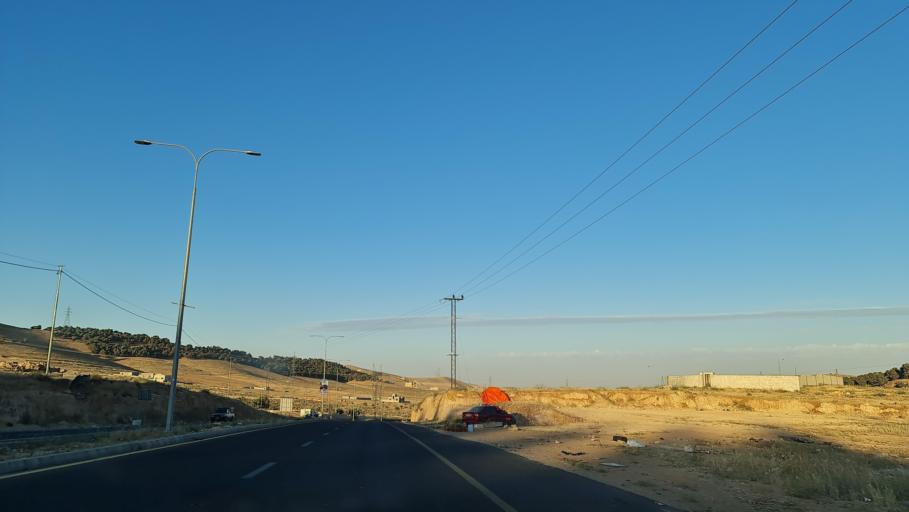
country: JO
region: Zarqa
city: Russeifa
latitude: 32.0923
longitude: 35.9732
